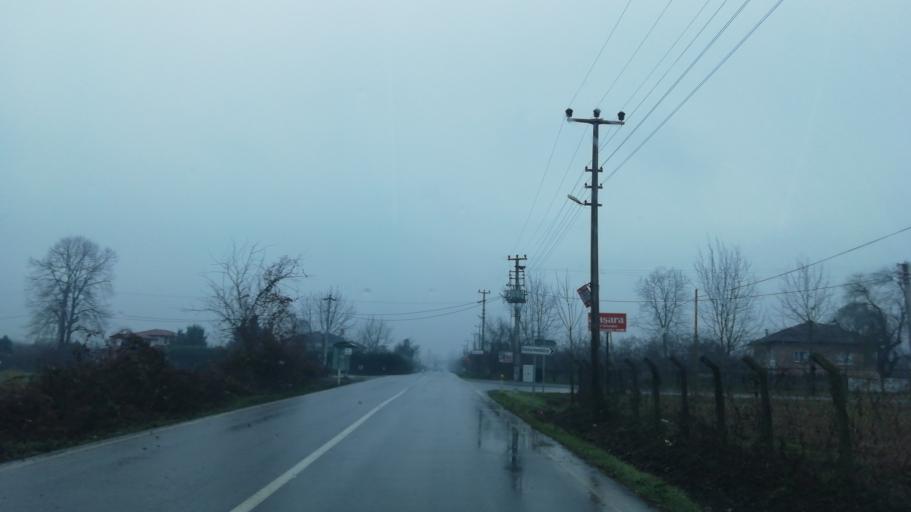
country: TR
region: Sakarya
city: Karapurcek
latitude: 40.6895
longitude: 30.4693
